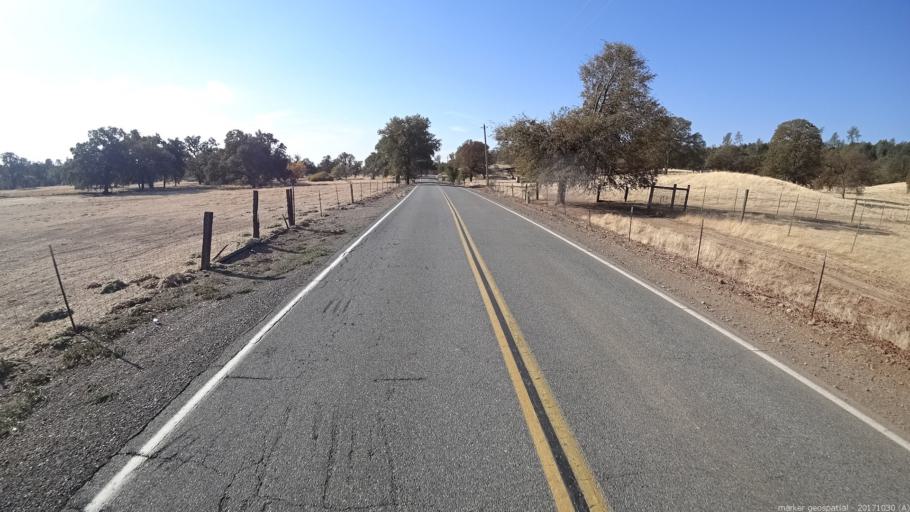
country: US
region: California
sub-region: Shasta County
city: Palo Cedro
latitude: 40.5902
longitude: -122.1743
